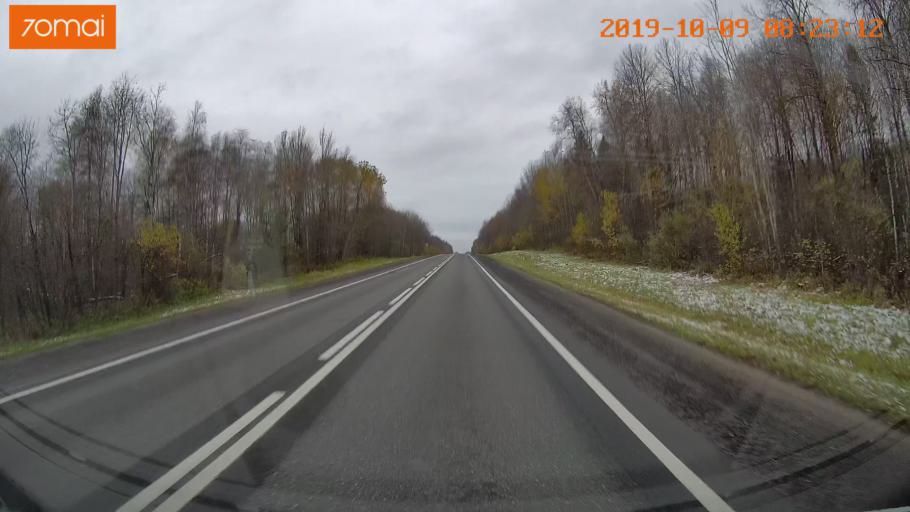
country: RU
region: Vologda
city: Gryazovets
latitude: 58.7513
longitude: 40.2847
